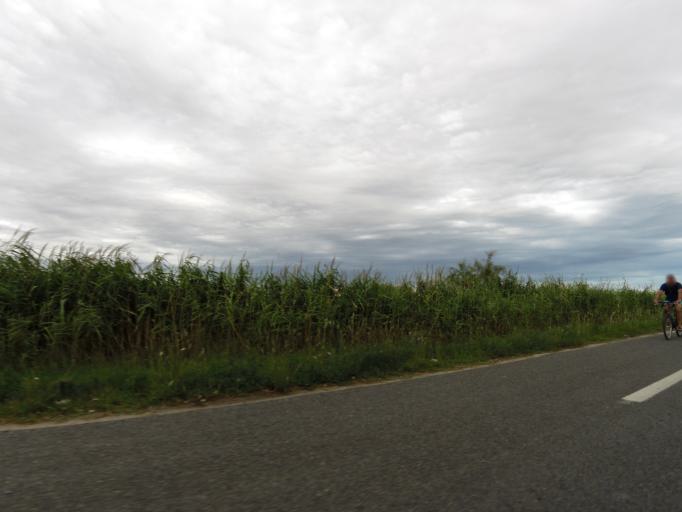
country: FR
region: Languedoc-Roussillon
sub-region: Departement du Gard
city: Le Grau-du-Roi
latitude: 43.5307
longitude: 4.1496
